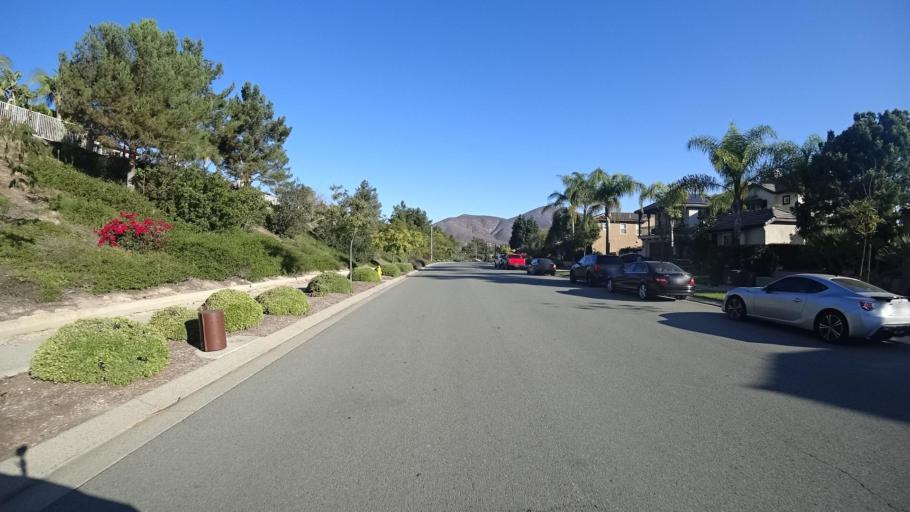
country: US
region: California
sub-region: San Diego County
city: La Presa
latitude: 32.6568
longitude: -116.9452
